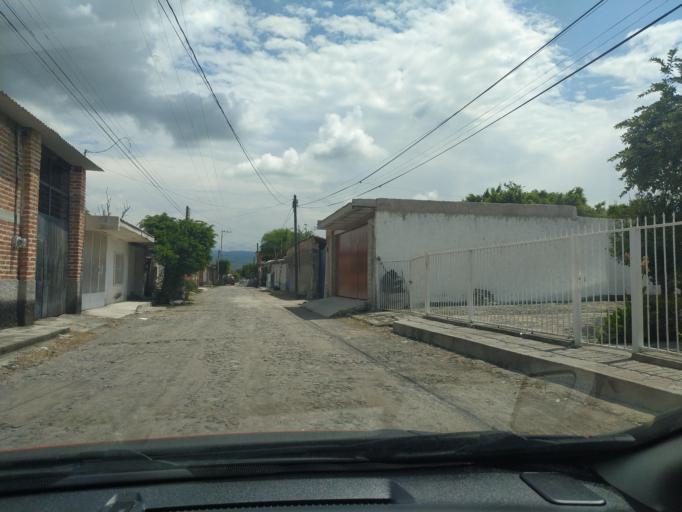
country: MX
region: Jalisco
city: Villa Corona
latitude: 20.3485
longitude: -103.6715
